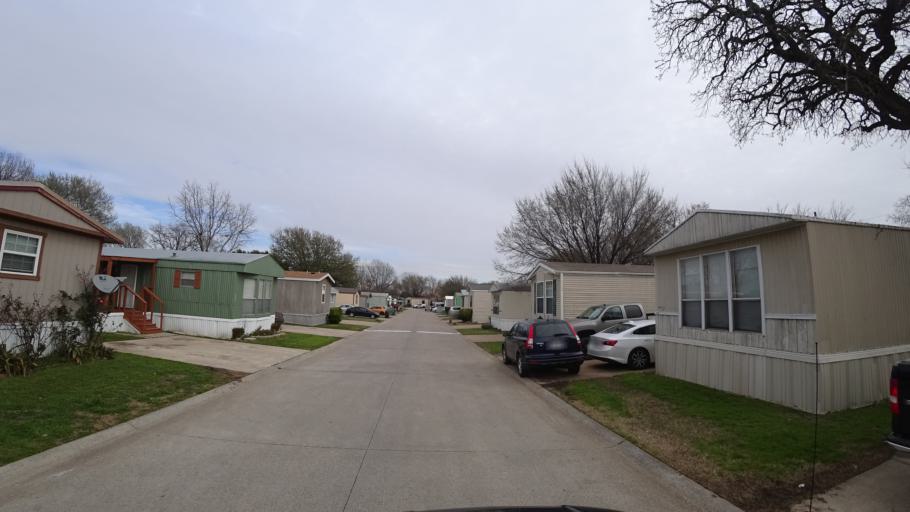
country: US
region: Texas
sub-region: Denton County
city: Lewisville
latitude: 33.0322
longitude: -96.9850
